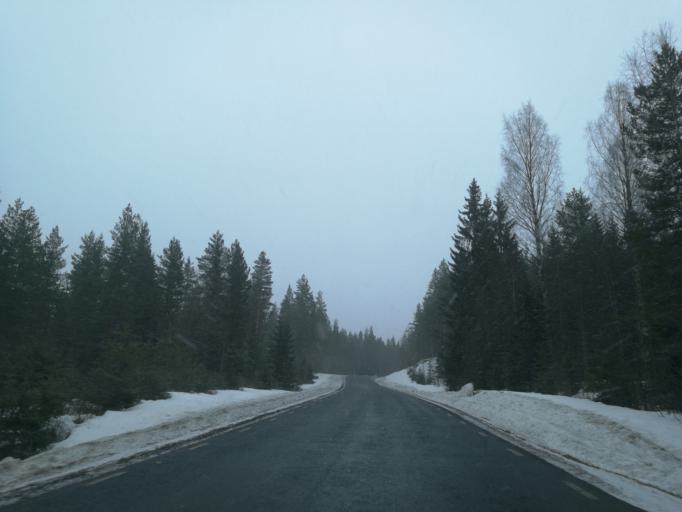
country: SE
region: Vaermland
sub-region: Torsby Kommun
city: Torsby
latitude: 60.6684
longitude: 12.6957
